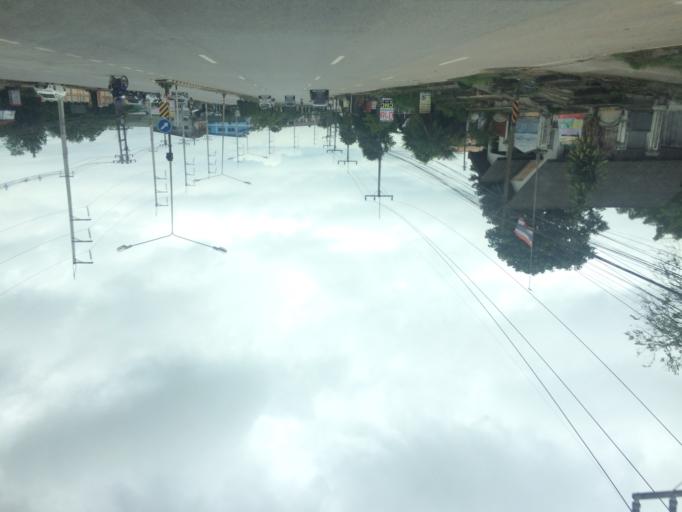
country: TH
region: Chiang Rai
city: Mae Chan
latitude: 20.1324
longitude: 99.8621
